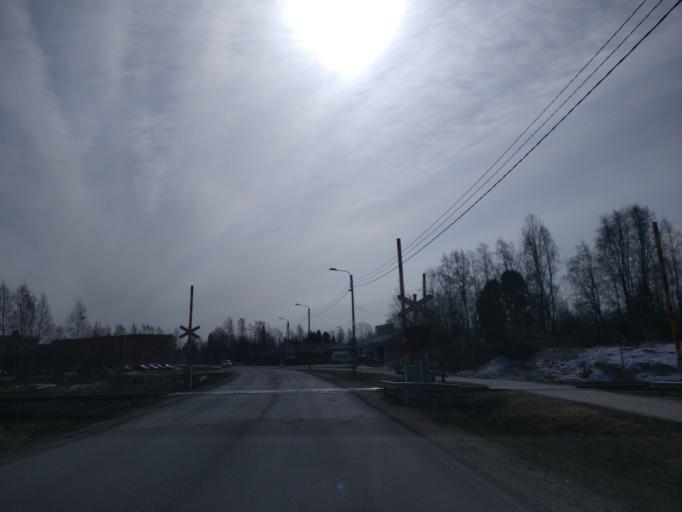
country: FI
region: Lapland
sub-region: Kemi-Tornio
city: Kemi
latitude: 65.7523
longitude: 24.5544
